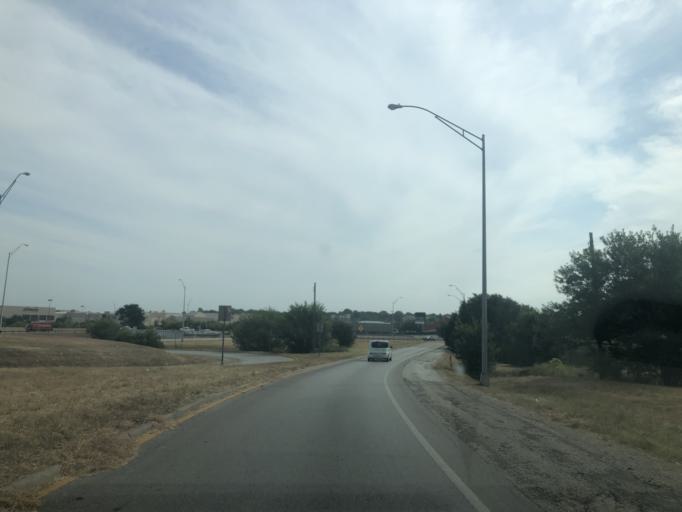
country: US
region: Texas
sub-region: Tarrant County
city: White Settlement
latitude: 32.7348
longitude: -97.4401
